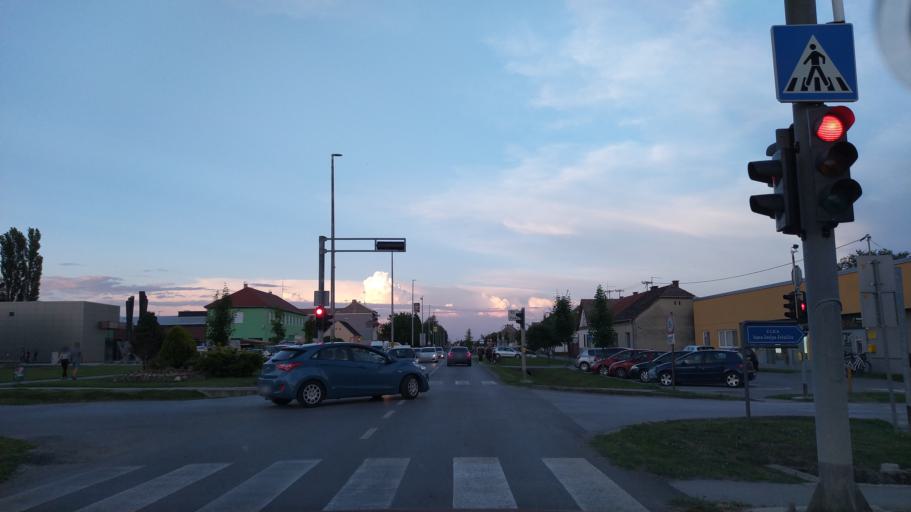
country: HR
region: Osjecko-Baranjska
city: Cepin
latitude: 45.5233
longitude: 18.5635
